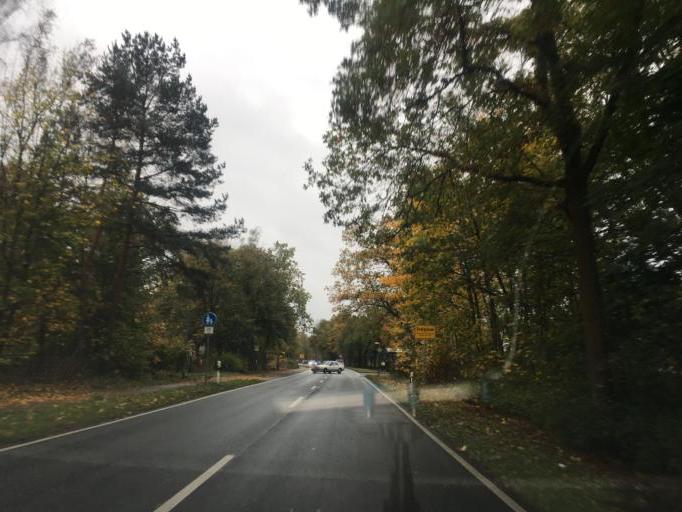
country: DE
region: Lower Saxony
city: Winsen
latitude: 52.6375
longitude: 9.9311
